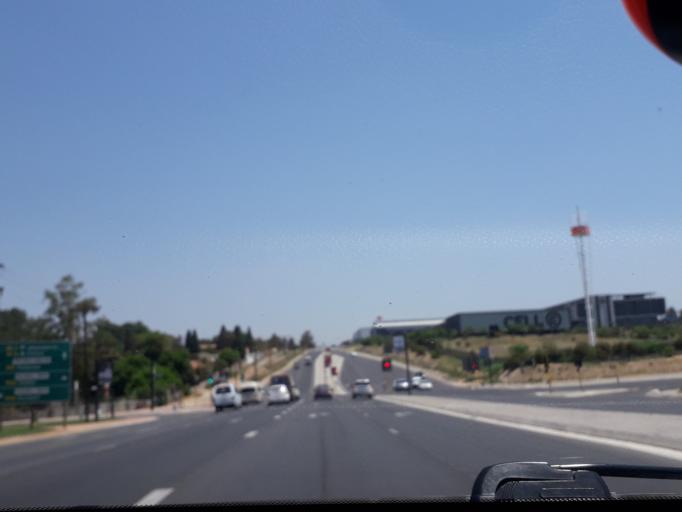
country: ZA
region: Gauteng
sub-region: City of Johannesburg Metropolitan Municipality
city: Midrand
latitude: -26.0417
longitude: 28.1057
